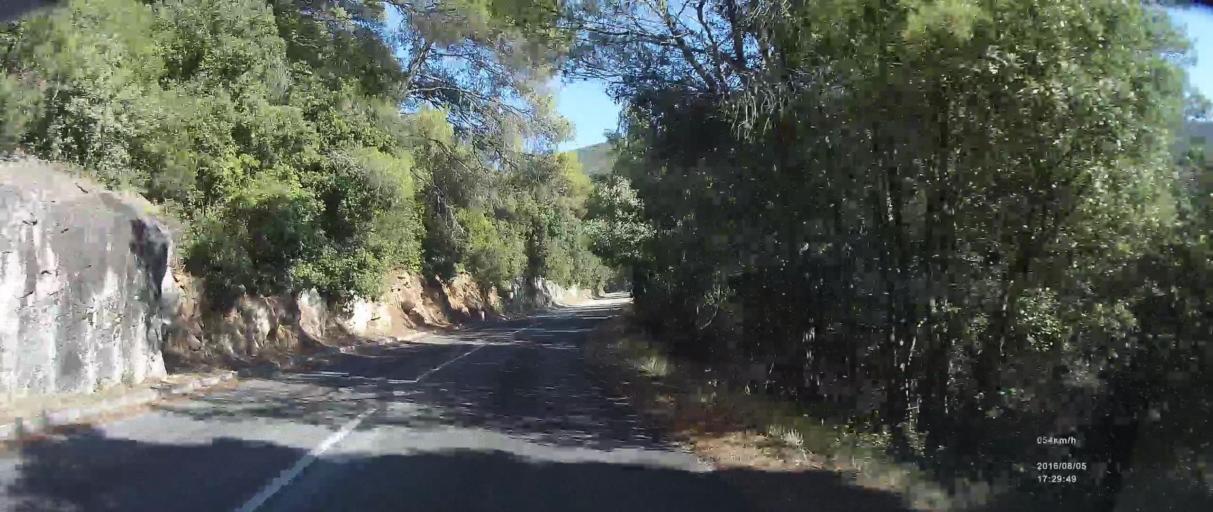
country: HR
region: Dubrovacko-Neretvanska
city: Blato
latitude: 42.7771
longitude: 17.4112
